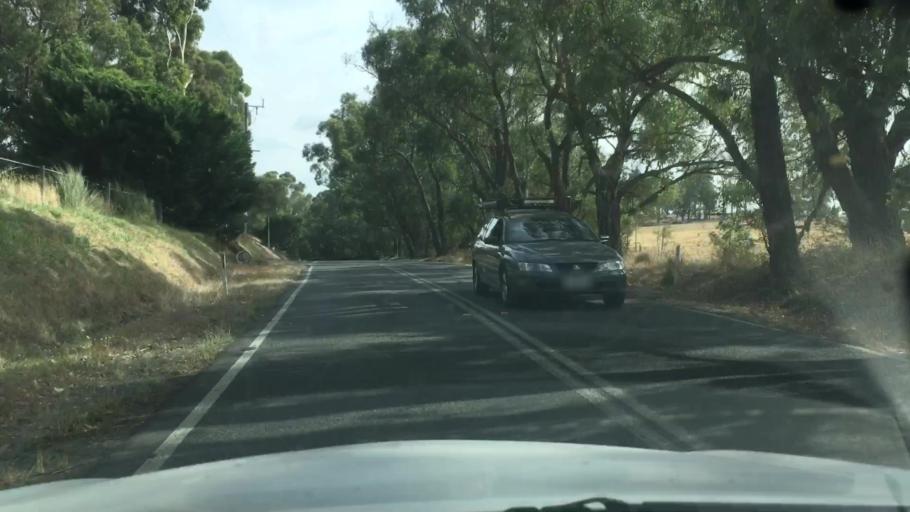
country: AU
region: Victoria
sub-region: Yarra Ranges
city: Macclesfield
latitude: -37.8710
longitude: 145.4792
